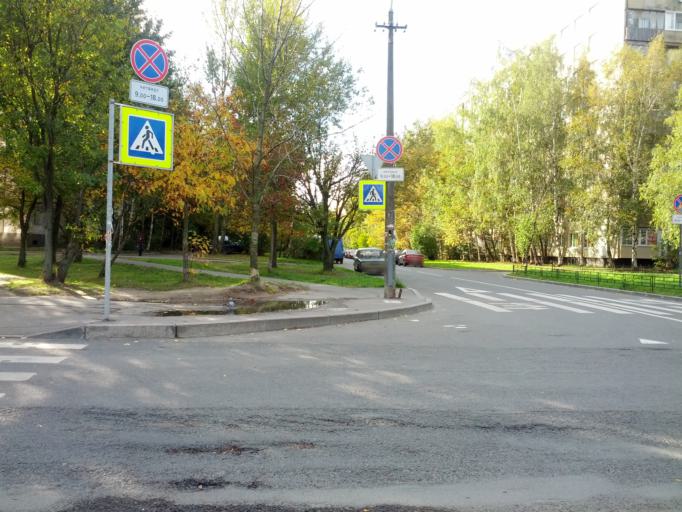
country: RU
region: Leningrad
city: Rybatskoye
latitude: 59.9023
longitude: 30.4863
